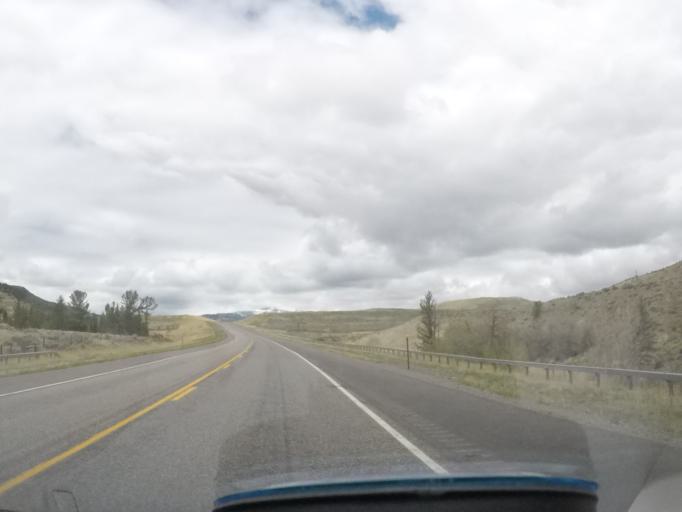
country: US
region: Wyoming
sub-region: Sublette County
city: Pinedale
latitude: 43.5822
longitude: -109.7648
